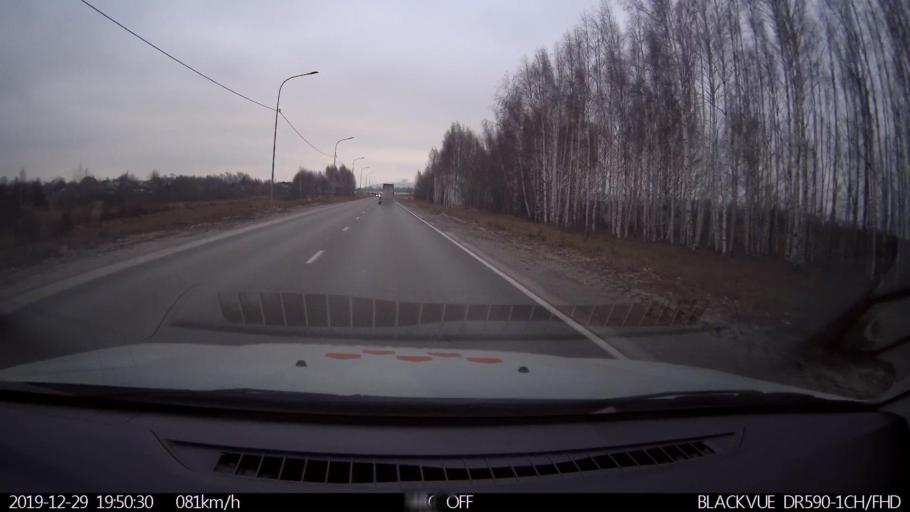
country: RU
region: Nizjnij Novgorod
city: Bor
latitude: 56.3673
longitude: 44.0290
